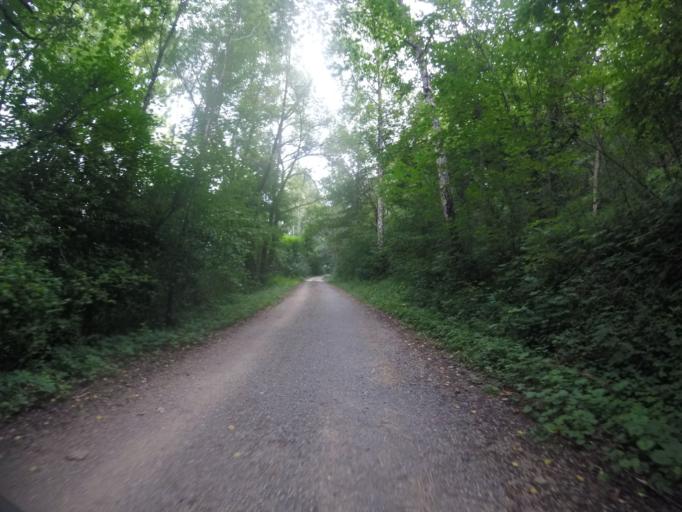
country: DE
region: Baden-Wuerttemberg
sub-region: Regierungsbezirk Stuttgart
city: Lorch
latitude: 48.7942
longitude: 9.6740
